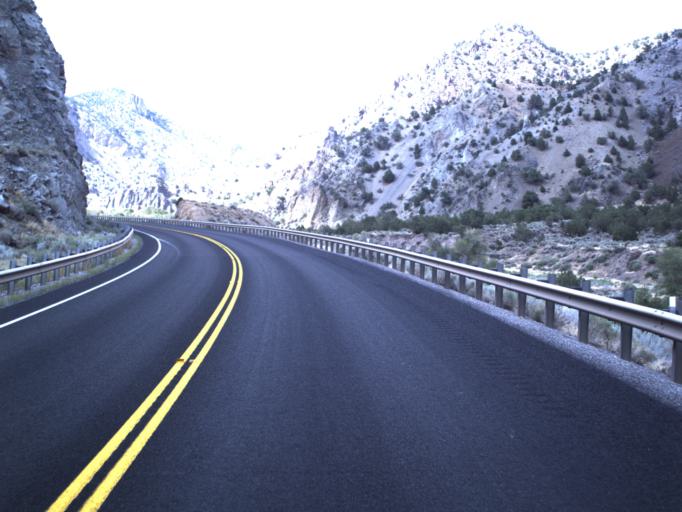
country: US
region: Utah
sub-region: Sevier County
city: Monroe
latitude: 38.5489
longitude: -112.2682
